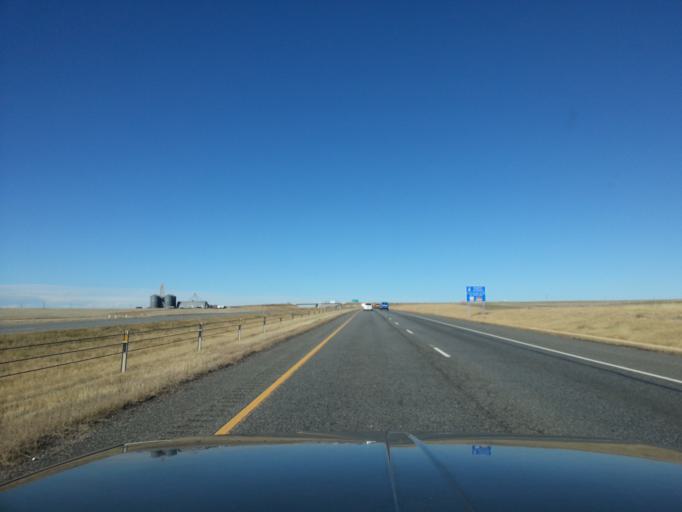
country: US
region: Colorado
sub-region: Adams County
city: Aurora
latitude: 39.8483
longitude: -104.7467
